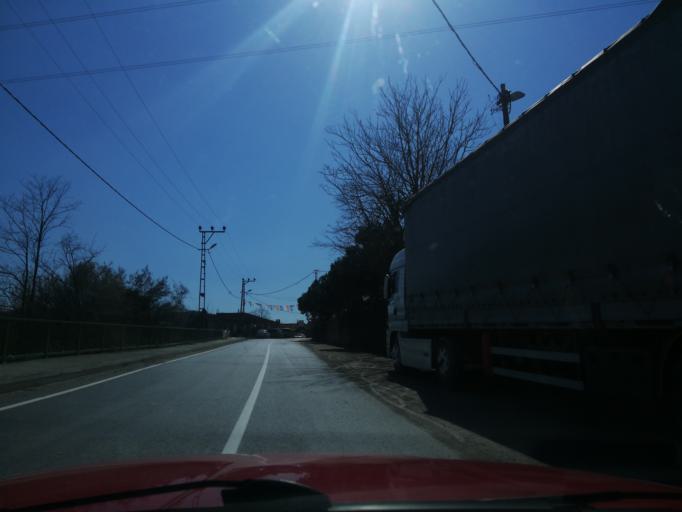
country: TR
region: Istanbul
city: Mahmut Sevket Pasa
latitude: 41.1284
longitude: 29.1600
